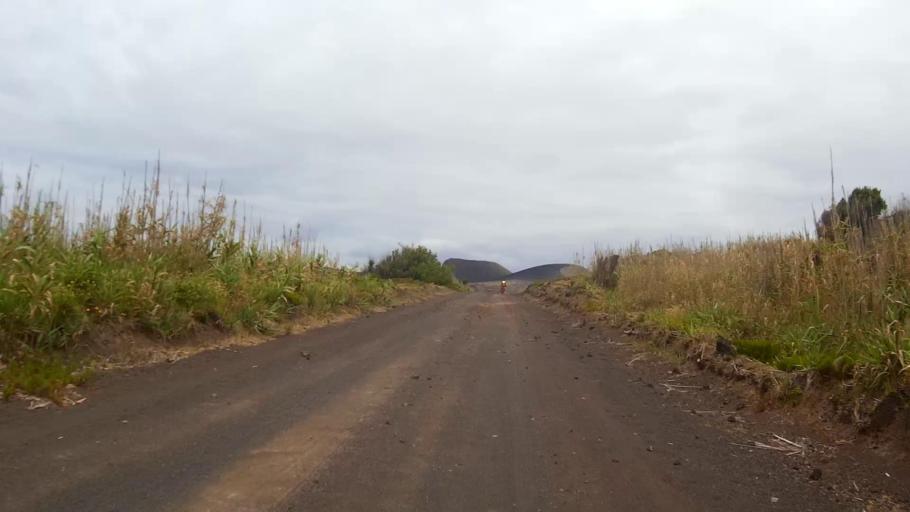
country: PT
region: Azores
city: Ribeira Grande
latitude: 38.5880
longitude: -28.8218
